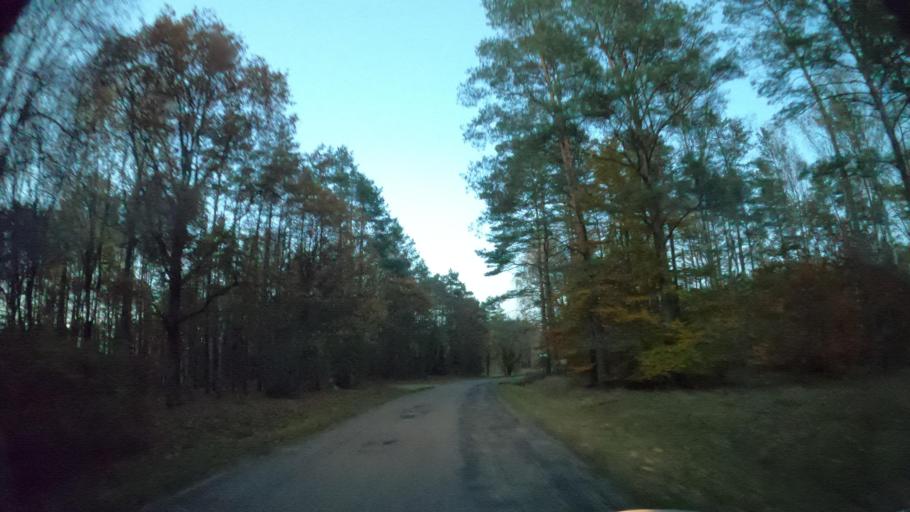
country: PL
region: Greater Poland Voivodeship
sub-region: Powiat zlotowski
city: Sypniewo
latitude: 53.4088
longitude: 16.5849
